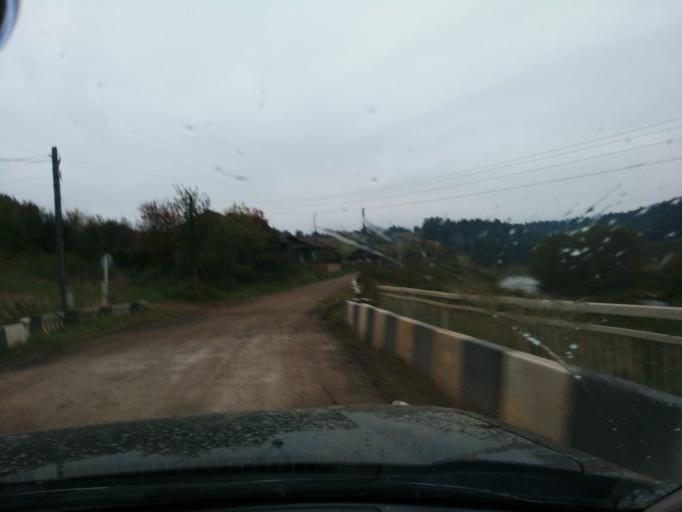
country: RU
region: Sverdlovsk
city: Sylva
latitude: 57.8602
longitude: 58.6309
